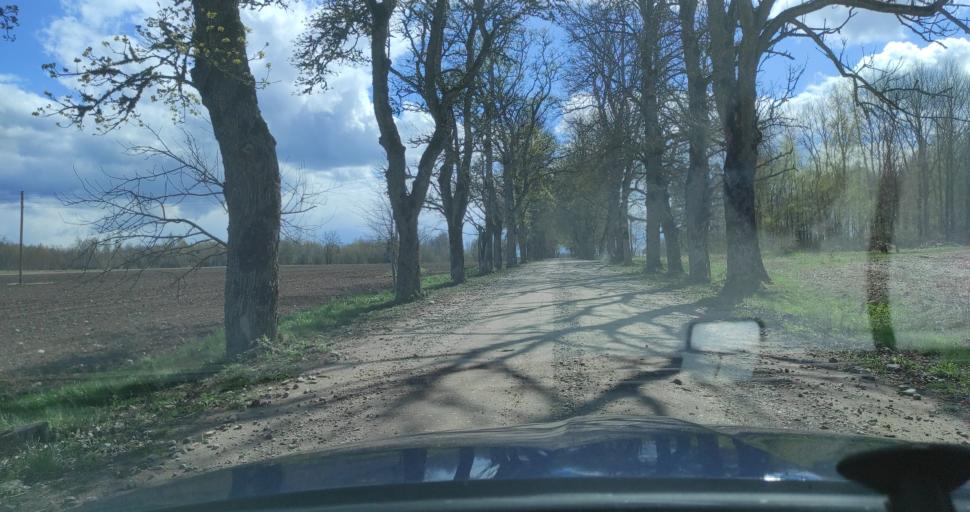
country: LV
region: Kuldigas Rajons
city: Kuldiga
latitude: 56.8603
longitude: 21.8134
